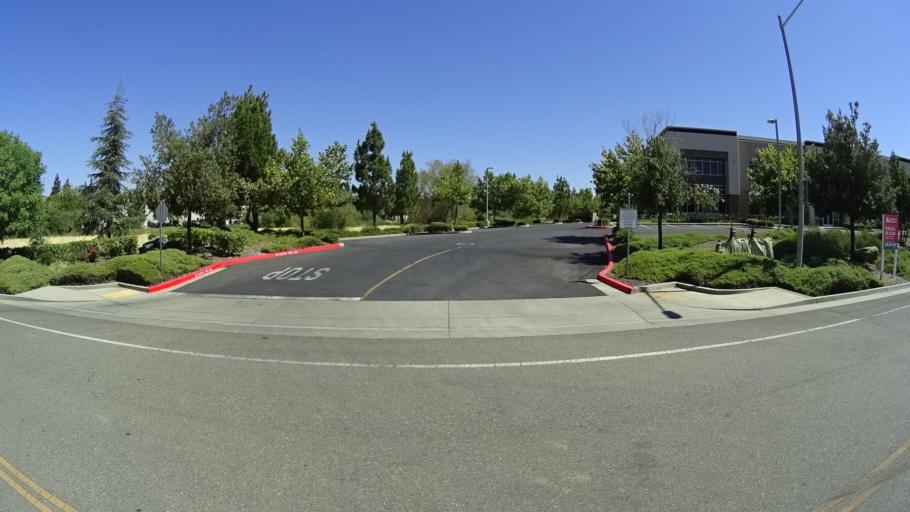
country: US
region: California
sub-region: Placer County
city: Roseville
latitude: 38.8124
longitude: -121.2939
